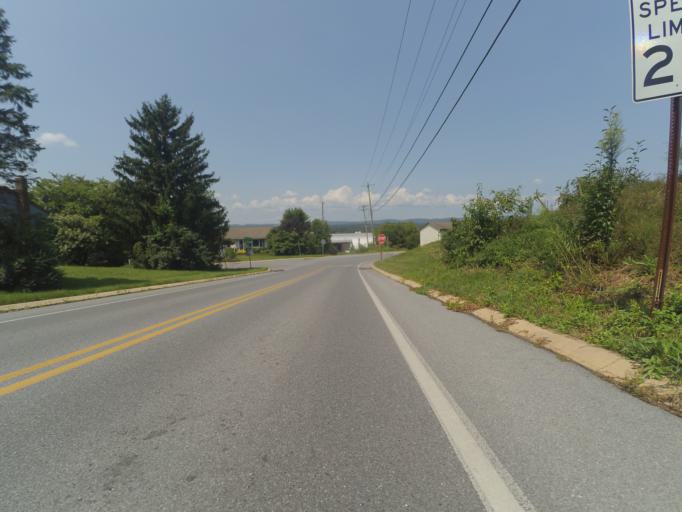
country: US
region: Pennsylvania
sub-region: Centre County
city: Houserville
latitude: 40.8303
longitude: -77.8119
